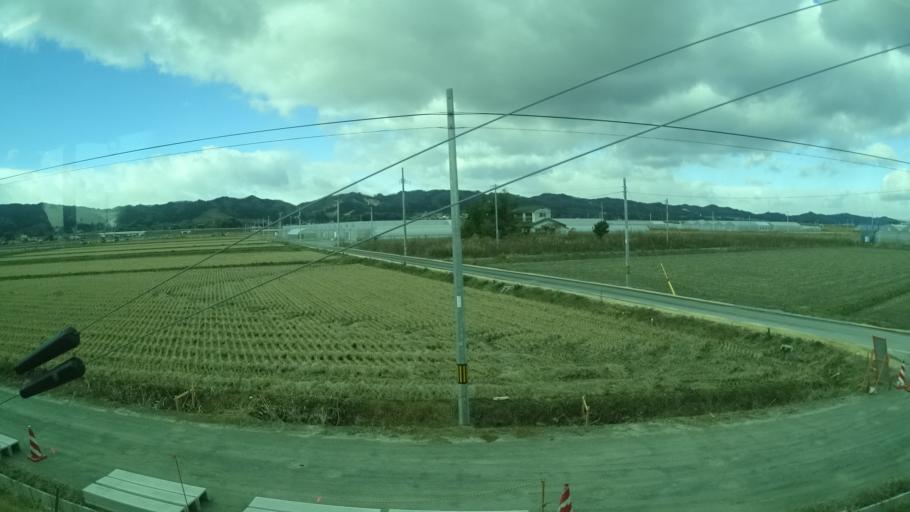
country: JP
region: Miyagi
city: Watari
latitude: 37.9828
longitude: 140.8888
